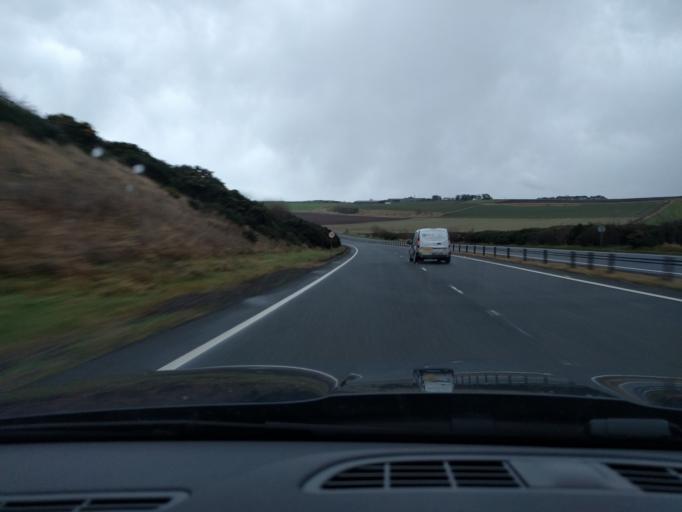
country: GB
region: Scotland
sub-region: East Lothian
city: East Linton
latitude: 55.9782
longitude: -2.6733
